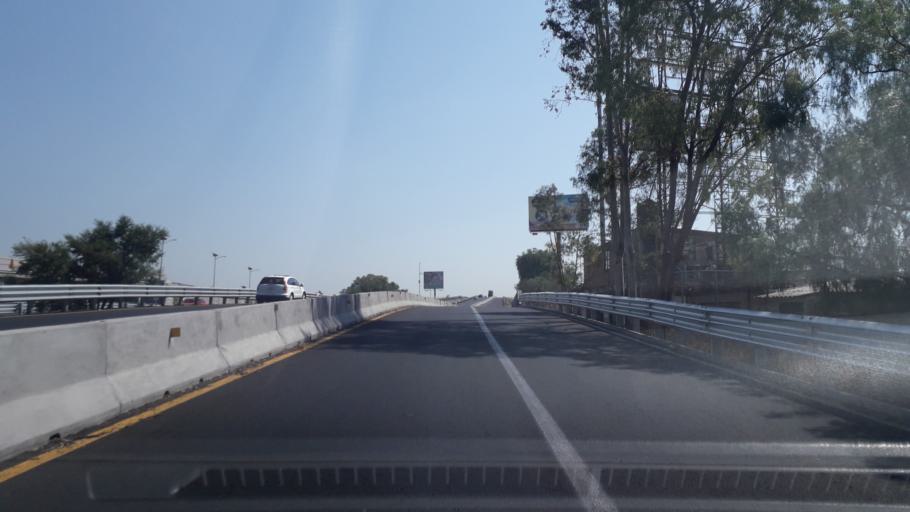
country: MX
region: Mexico
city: Santo Tomas Chiconautla
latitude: 19.6603
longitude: -99.0070
